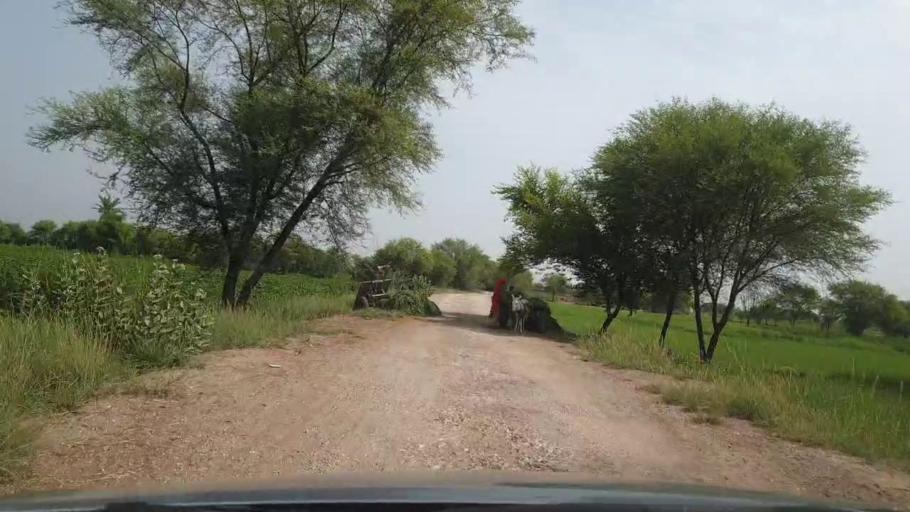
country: PK
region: Sindh
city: Rohri
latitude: 27.6515
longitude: 69.0234
